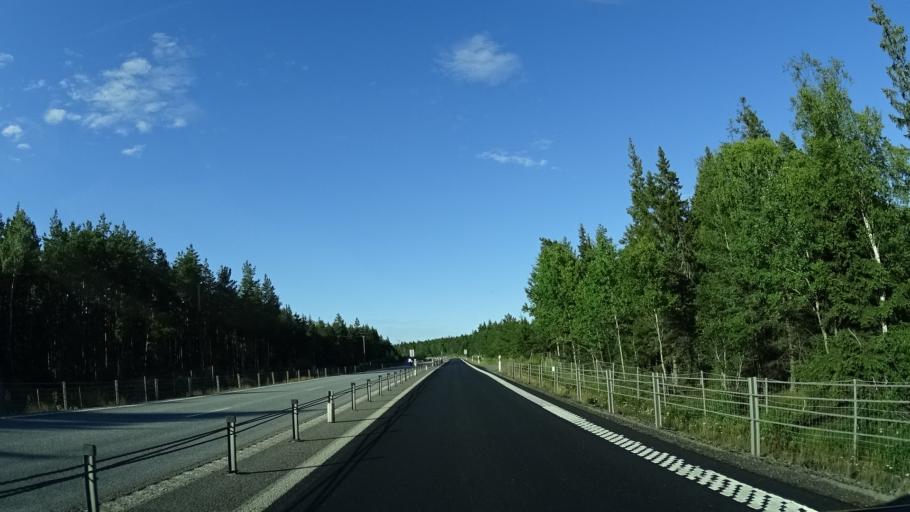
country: SE
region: Stockholm
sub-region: Osterakers Kommun
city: Akersberga
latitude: 59.5883
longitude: 18.2586
